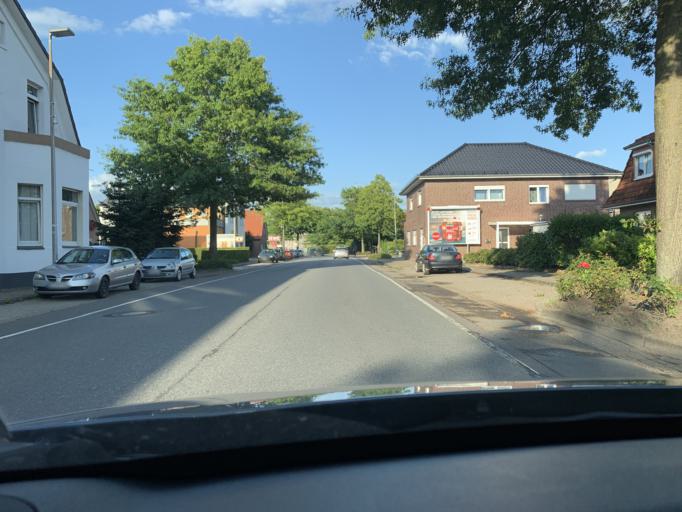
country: DE
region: Lower Saxony
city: Edewecht
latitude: 53.1197
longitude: 7.9734
